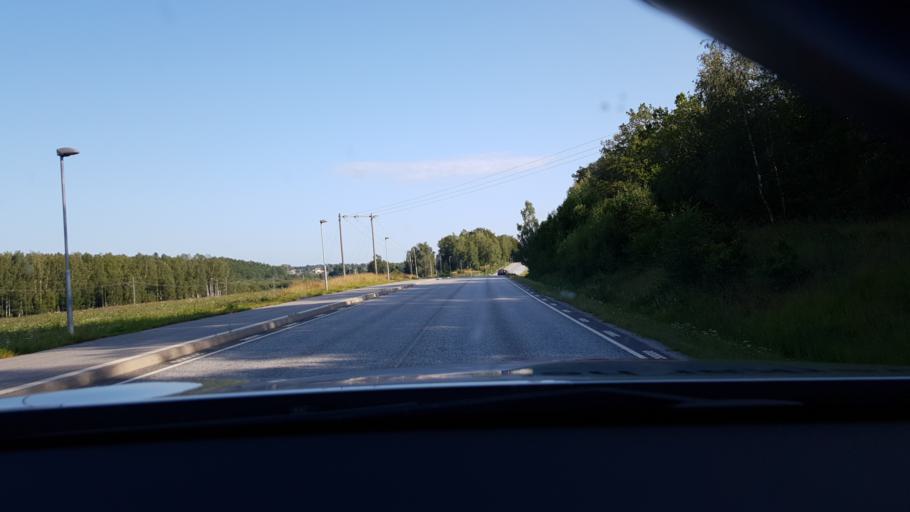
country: SE
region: Stockholm
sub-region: Nynashamns Kommun
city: Osmo
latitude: 58.9387
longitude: 17.9151
